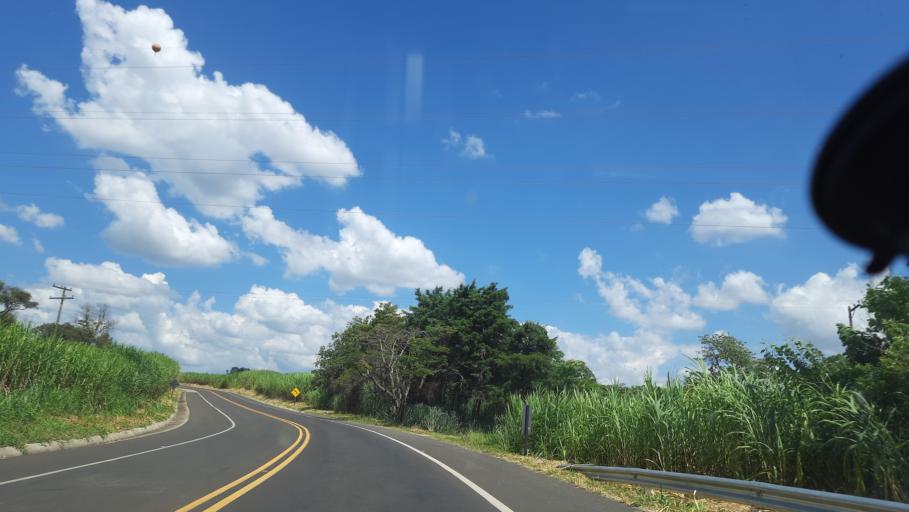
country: BR
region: Sao Paulo
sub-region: Sao Jose Do Rio Pardo
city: Sao Jose do Rio Pardo
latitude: -21.6068
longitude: -46.9666
